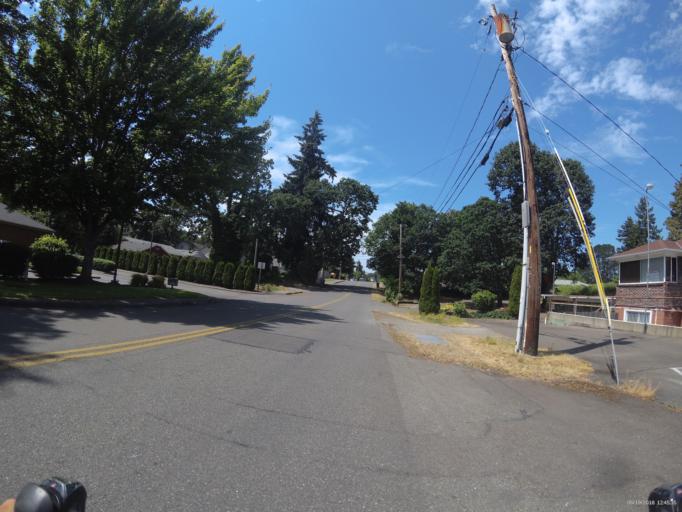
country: US
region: Washington
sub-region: Pierce County
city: Lakewood
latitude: 47.1635
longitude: -122.5210
